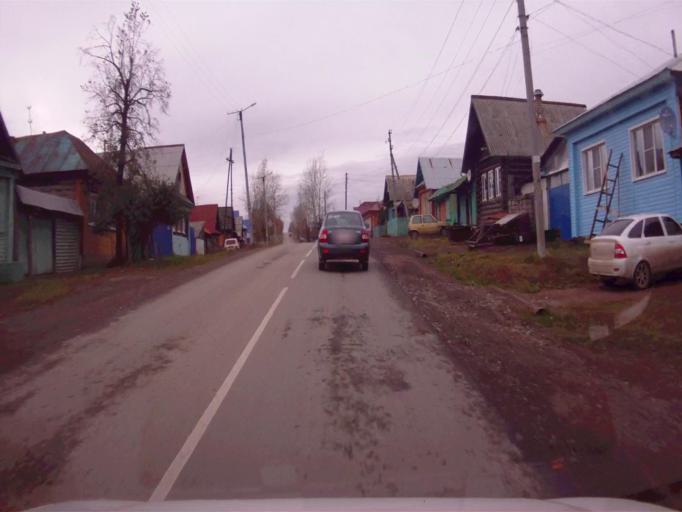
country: RU
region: Chelyabinsk
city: Nyazepetrovsk
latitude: 56.0583
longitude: 59.5846
